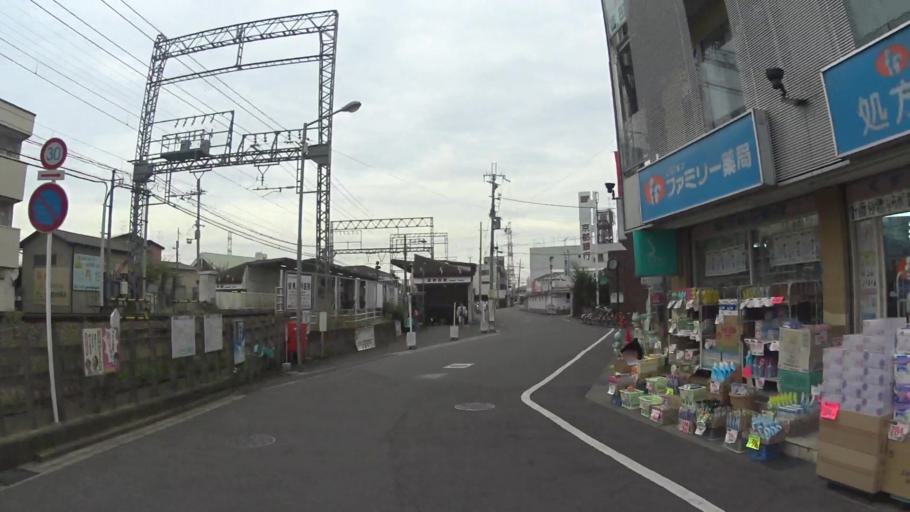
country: JP
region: Kyoto
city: Tanabe
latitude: 34.8394
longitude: 135.7732
